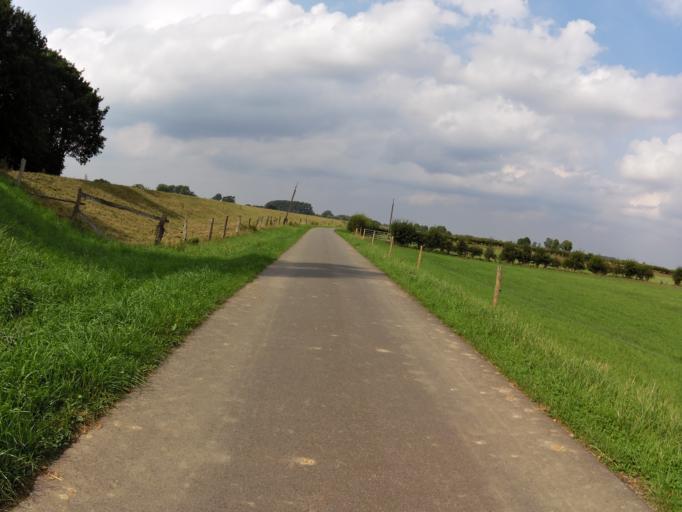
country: DE
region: Lower Saxony
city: Blender
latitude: 52.8951
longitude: 9.1674
